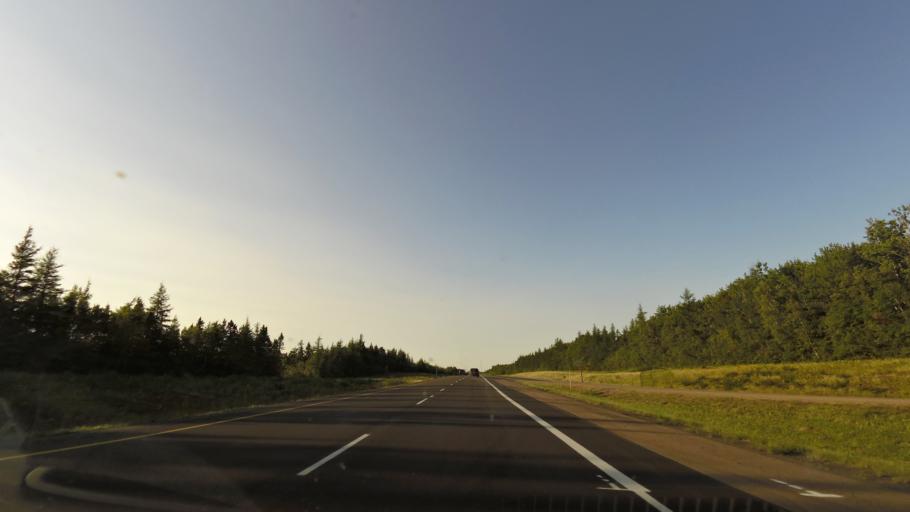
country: CA
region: New Brunswick
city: Dieppe
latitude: 46.0526
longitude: -64.5859
